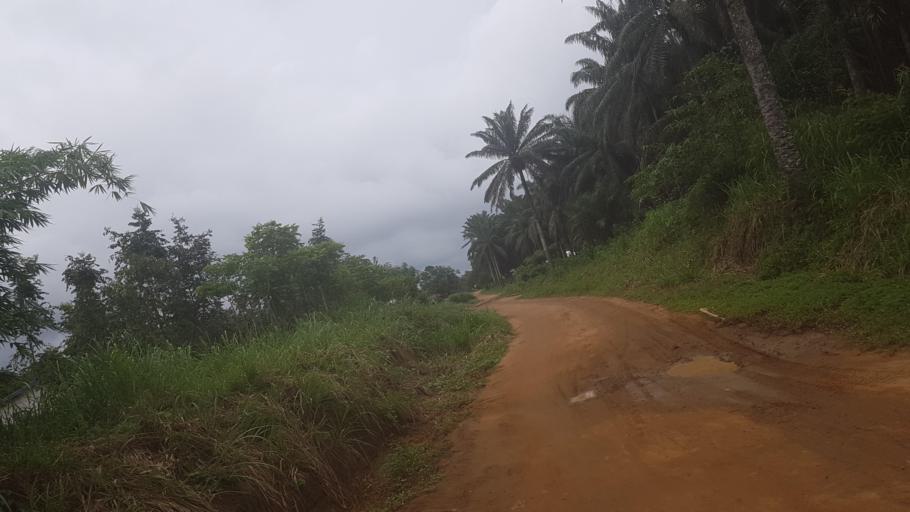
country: SL
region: Southern Province
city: Sumbuya
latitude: 7.5628
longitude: -12.1550
